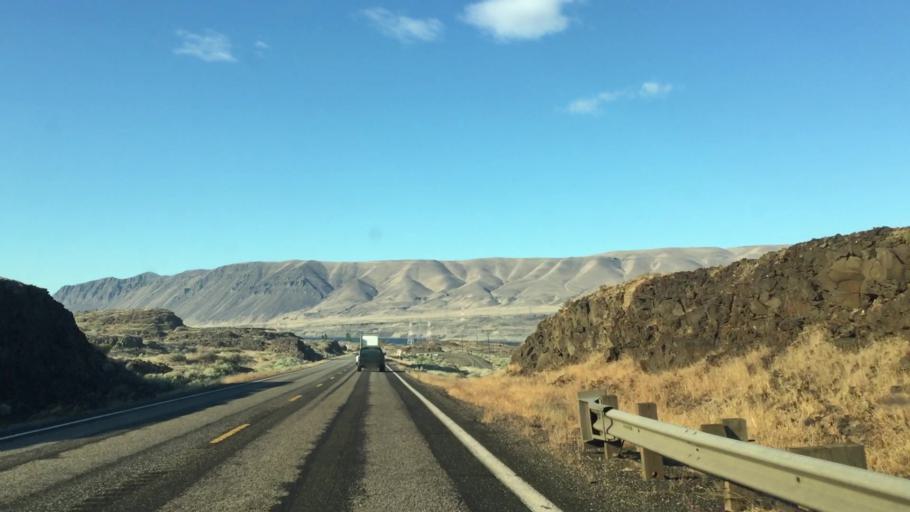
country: US
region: Washington
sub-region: Grant County
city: Mattawa
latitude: 46.8945
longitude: -119.9531
